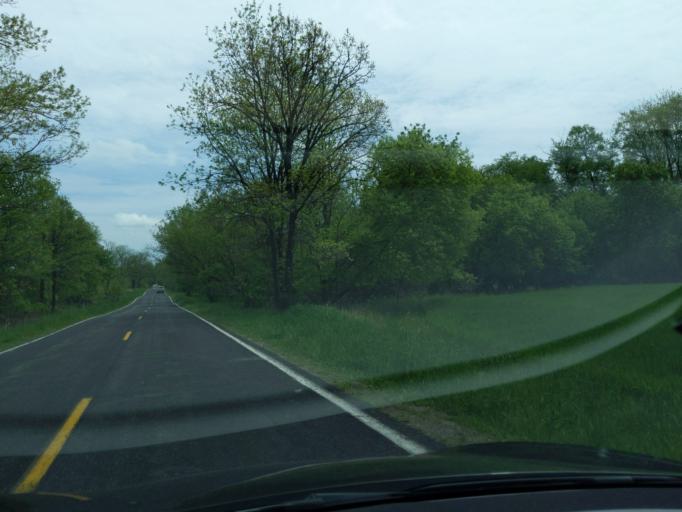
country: US
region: Michigan
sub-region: Ingham County
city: Stockbridge
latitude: 42.4684
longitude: -84.1743
